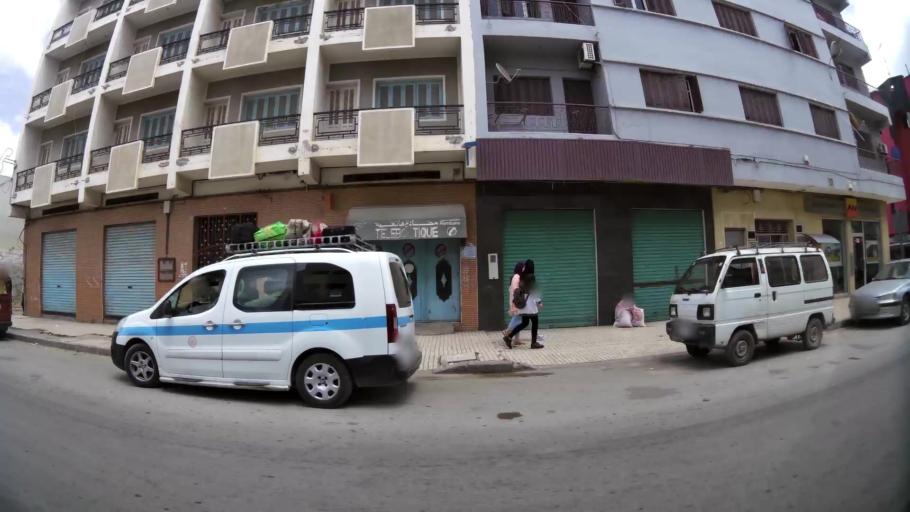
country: MA
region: Oriental
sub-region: Nador
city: Nador
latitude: 35.1743
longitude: -2.9209
